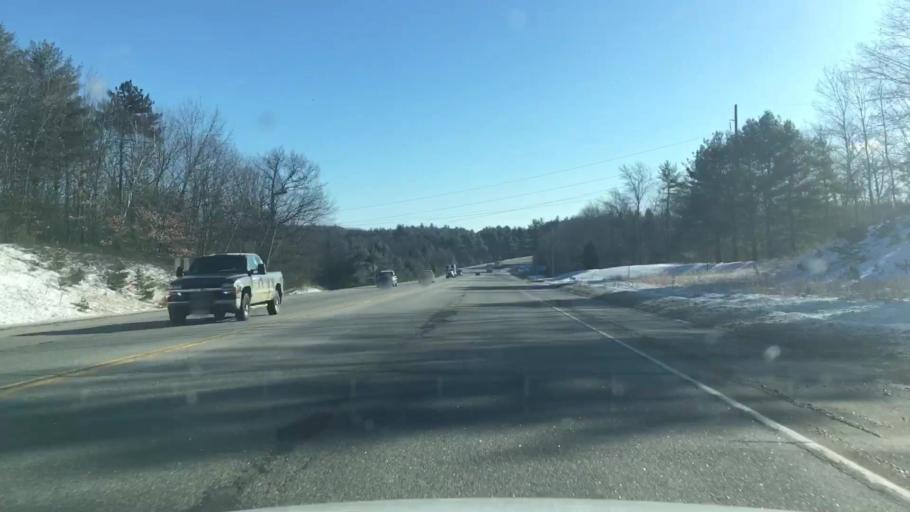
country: US
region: Maine
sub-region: Androscoggin County
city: Turner
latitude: 44.1836
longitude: -70.2346
